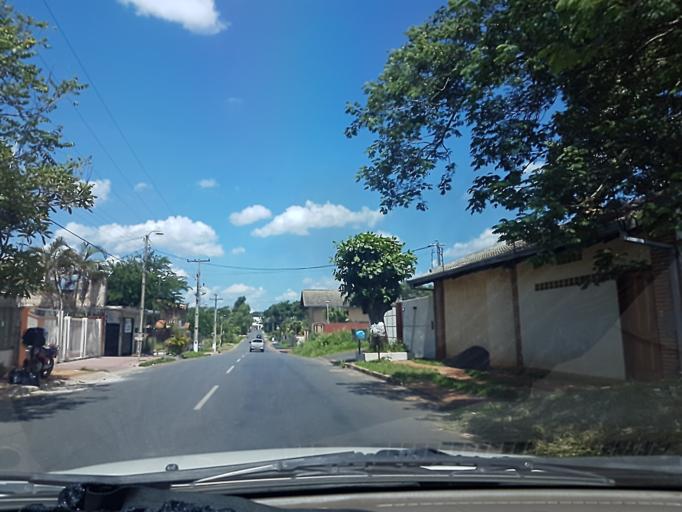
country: PY
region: Central
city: San Lorenzo
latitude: -25.2588
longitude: -57.5071
